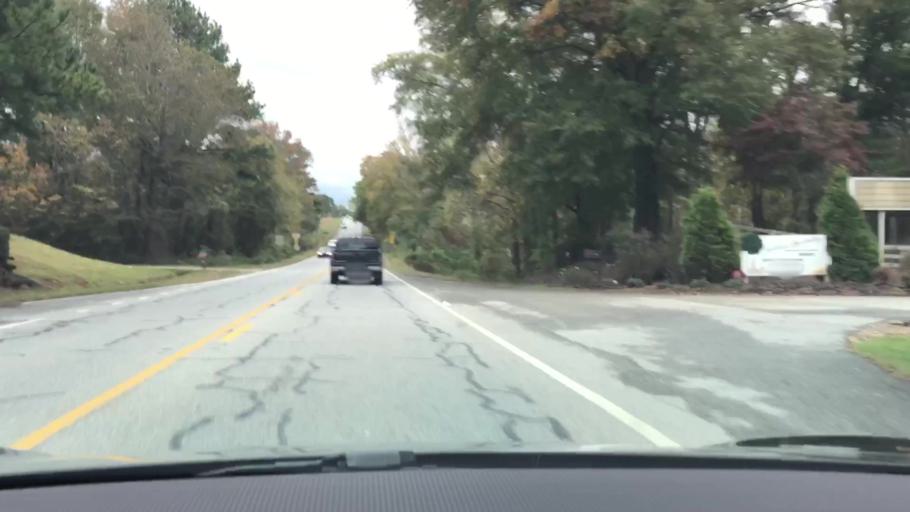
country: US
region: Georgia
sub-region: Oconee County
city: Watkinsville
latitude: 33.8510
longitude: -83.3965
